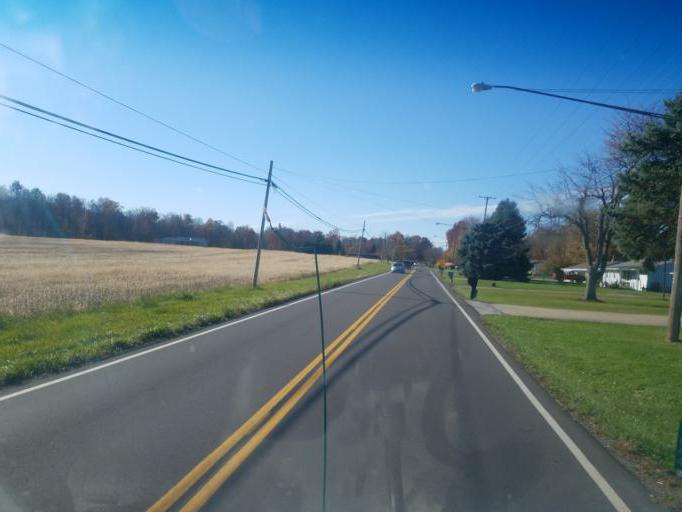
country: US
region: Ohio
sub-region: Richland County
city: Ontario
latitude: 40.7861
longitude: -82.5731
